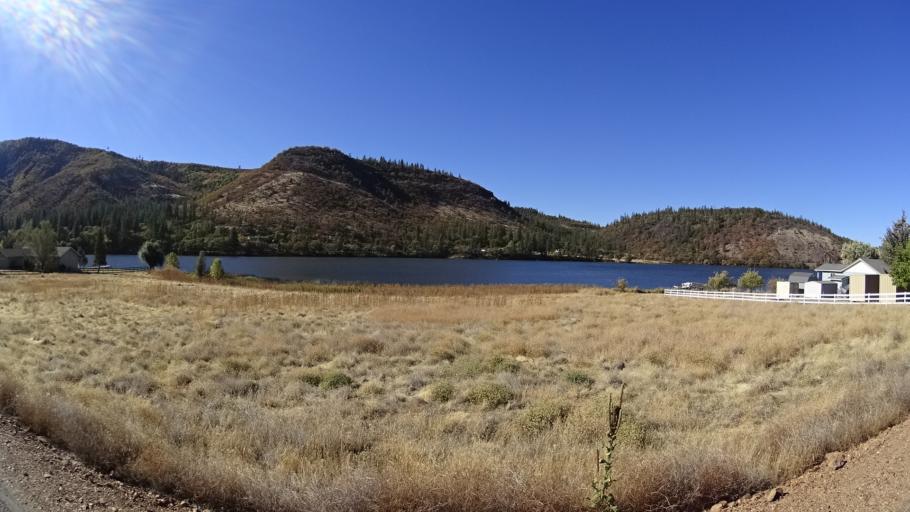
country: US
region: California
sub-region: Siskiyou County
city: Montague
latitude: 41.9715
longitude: -122.2753
